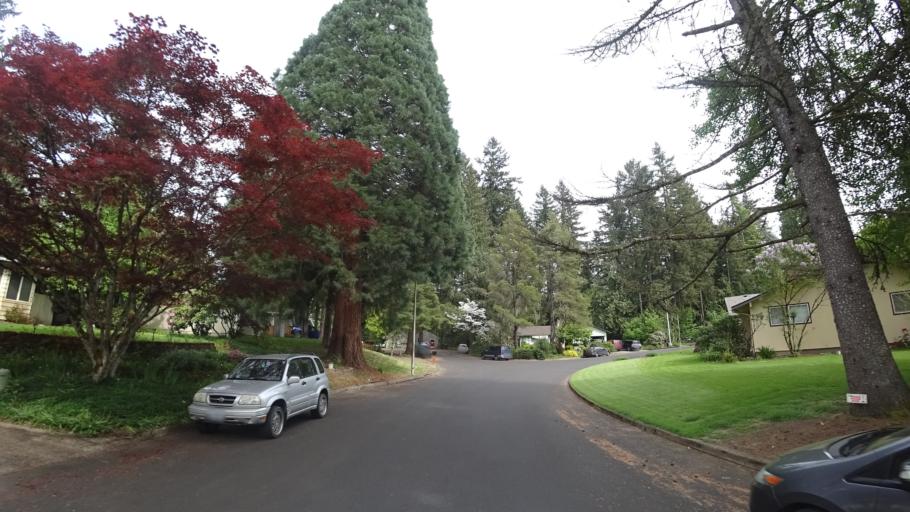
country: US
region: Oregon
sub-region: Washington County
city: Hillsboro
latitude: 45.5106
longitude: -122.9441
